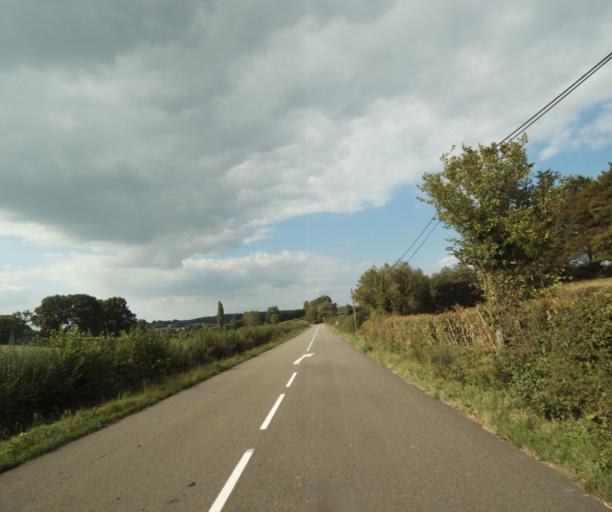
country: FR
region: Bourgogne
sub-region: Departement de Saone-et-Loire
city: Palinges
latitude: 46.5101
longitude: 4.2597
